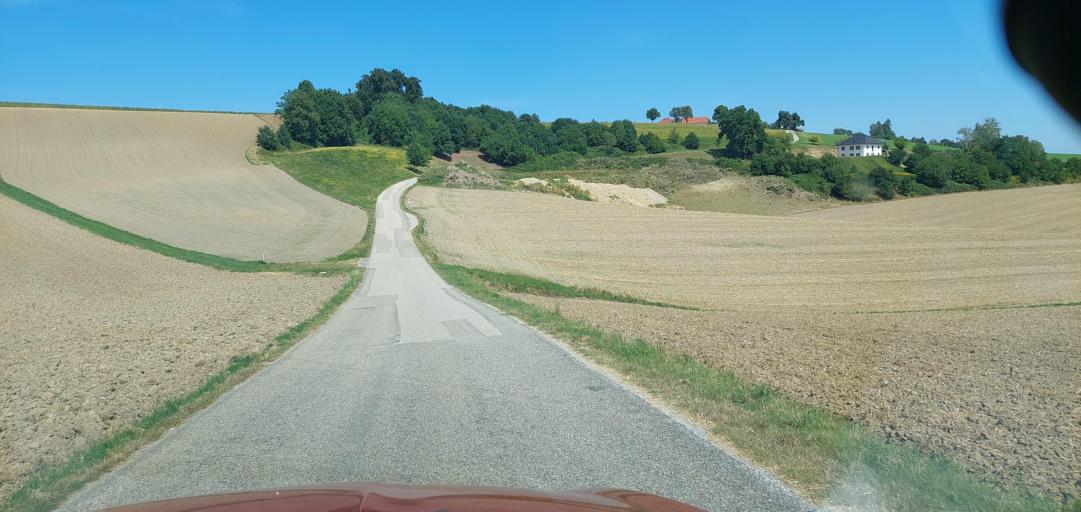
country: AT
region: Upper Austria
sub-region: Wels-Land
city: Offenhausen
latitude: 48.1393
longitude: 13.8381
